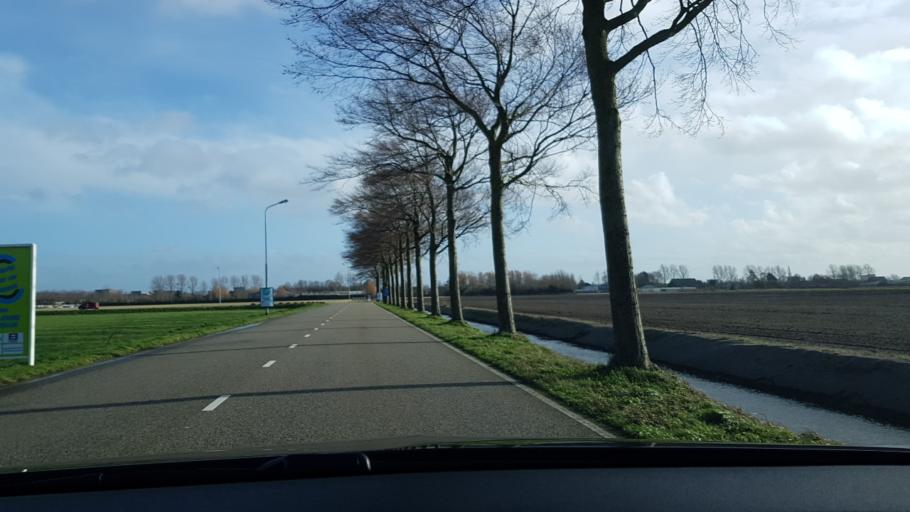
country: NL
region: North Holland
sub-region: Gemeente Heemstede
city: Heemstede
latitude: 52.3295
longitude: 4.6348
